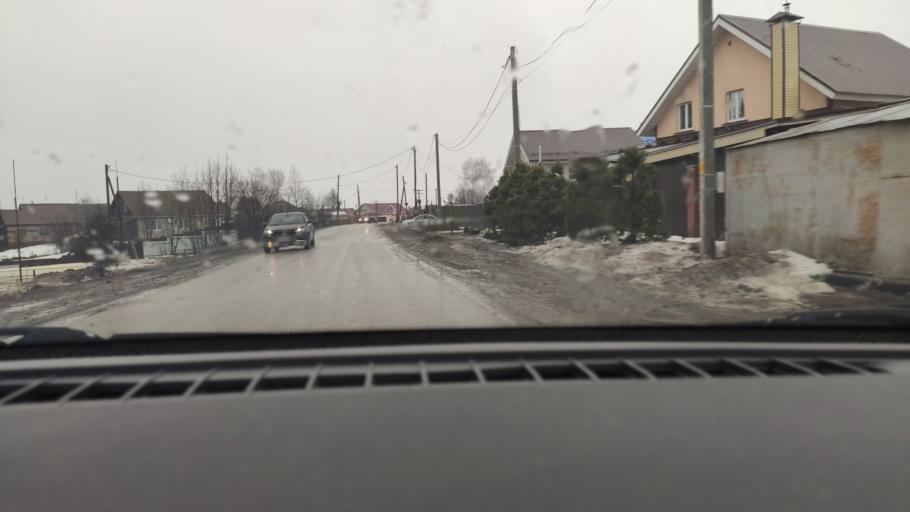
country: RU
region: Perm
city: Kultayevo
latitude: 57.9004
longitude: 55.9560
